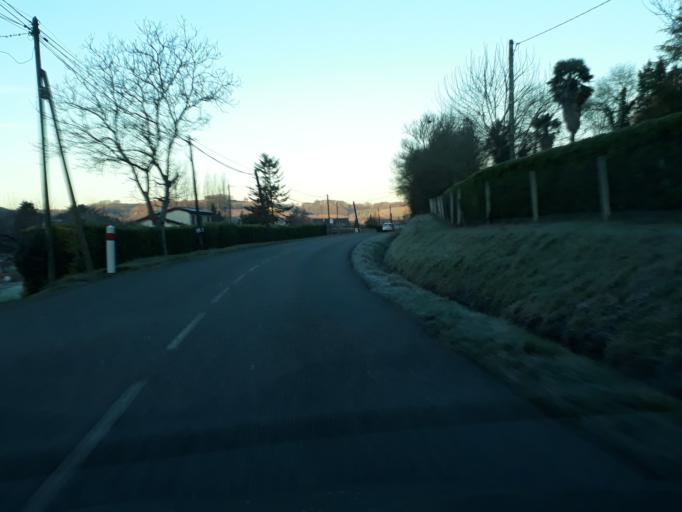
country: FR
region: Midi-Pyrenees
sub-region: Departement du Gers
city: Pavie
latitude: 43.6198
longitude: 0.6566
